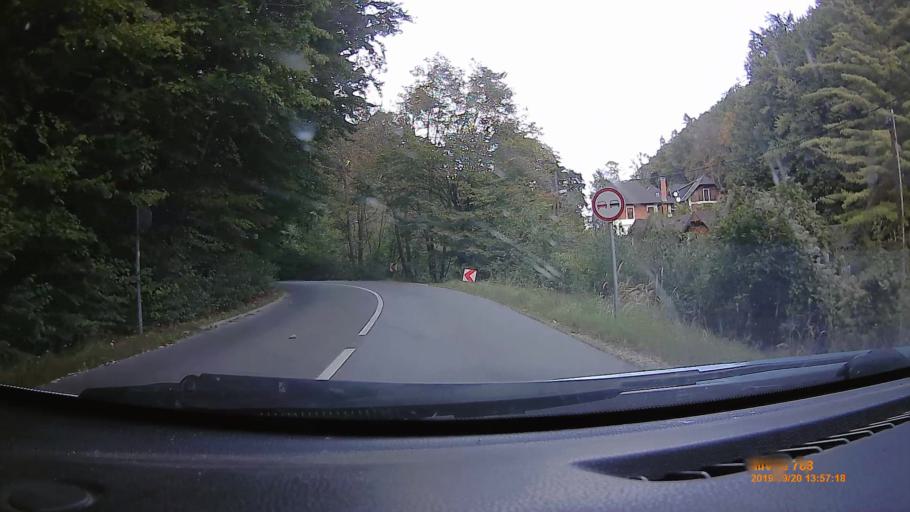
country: HU
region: Borsod-Abauj-Zemplen
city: Sajobabony
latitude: 48.0913
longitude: 20.6196
